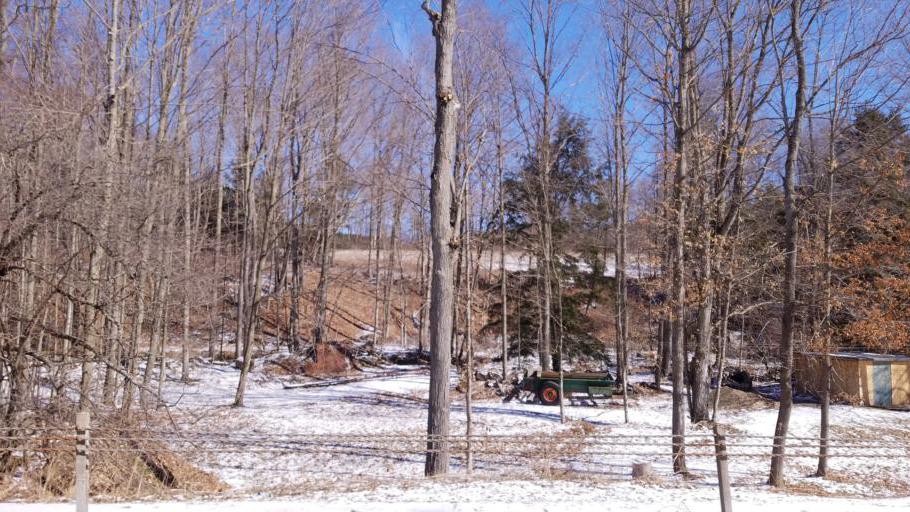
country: US
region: New York
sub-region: Allegany County
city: Andover
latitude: 42.0692
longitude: -77.8405
